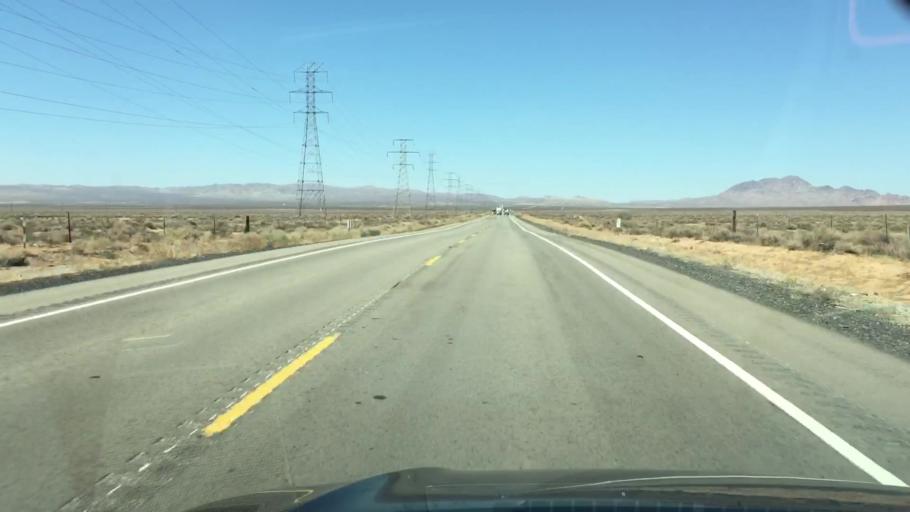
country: US
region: California
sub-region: Kern County
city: Boron
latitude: 35.1883
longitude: -117.5968
